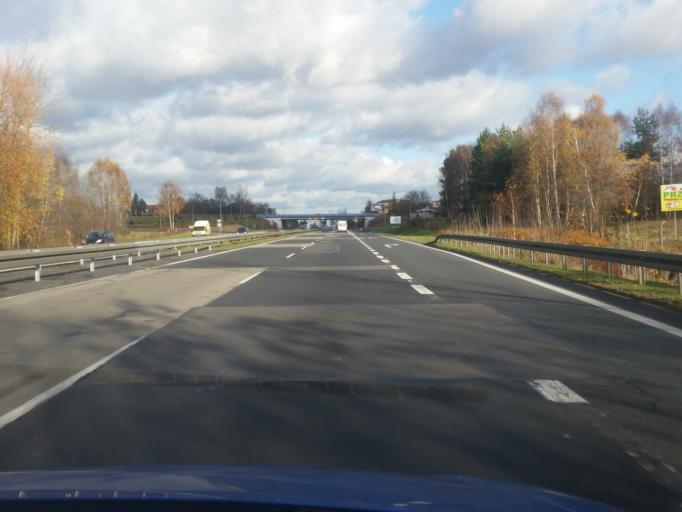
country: PL
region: Silesian Voivodeship
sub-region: Czestochowa
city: Czestochowa
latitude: 50.8447
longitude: 19.1496
